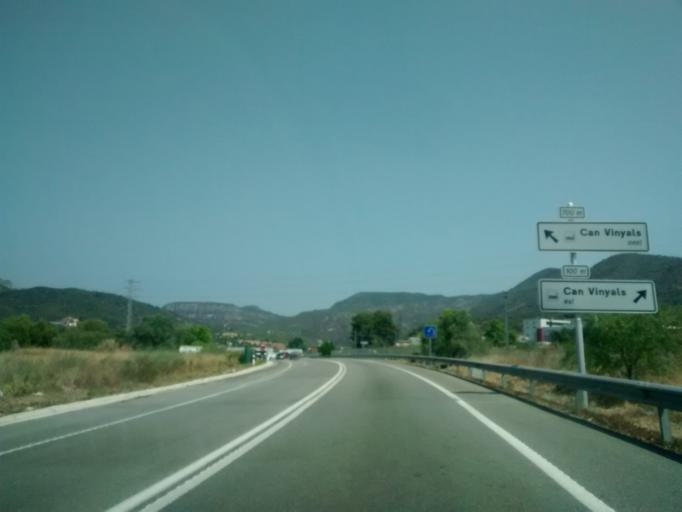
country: ES
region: Catalonia
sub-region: Provincia de Barcelona
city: Olesa de Montserrat
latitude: 41.5492
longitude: 1.8812
